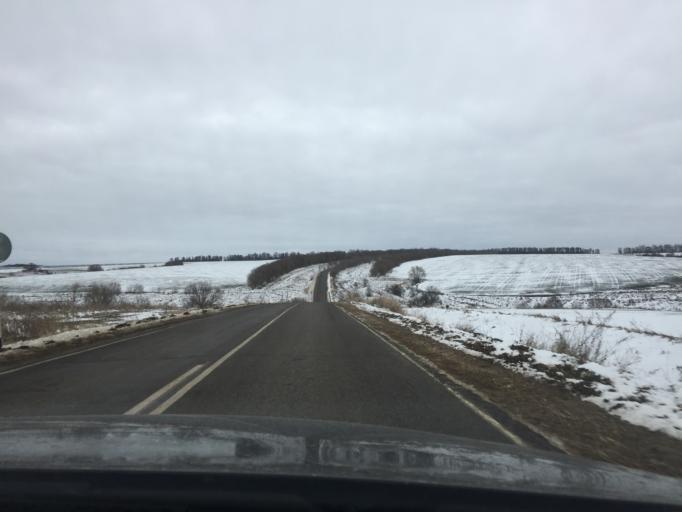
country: RU
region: Tula
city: Teploye
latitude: 53.8062
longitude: 37.5596
